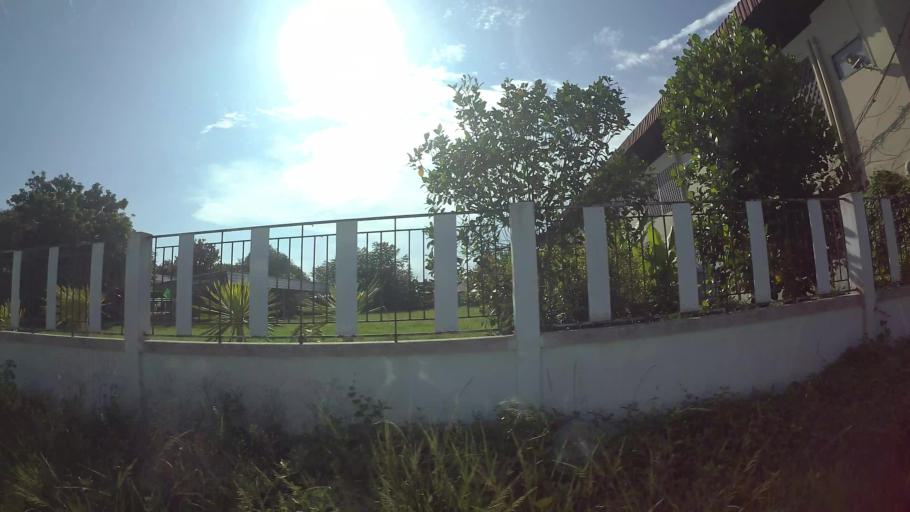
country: TH
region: Rayong
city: Rayong
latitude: 12.6711
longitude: 101.3013
